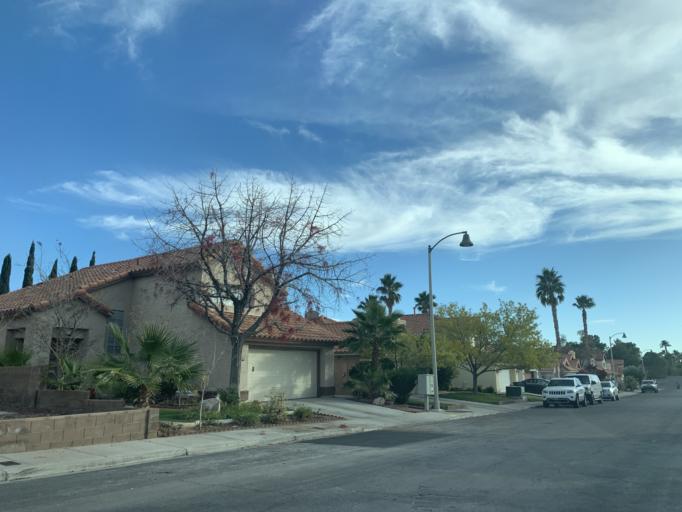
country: US
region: Nevada
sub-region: Clark County
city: Summerlin South
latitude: 36.1315
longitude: -115.3023
